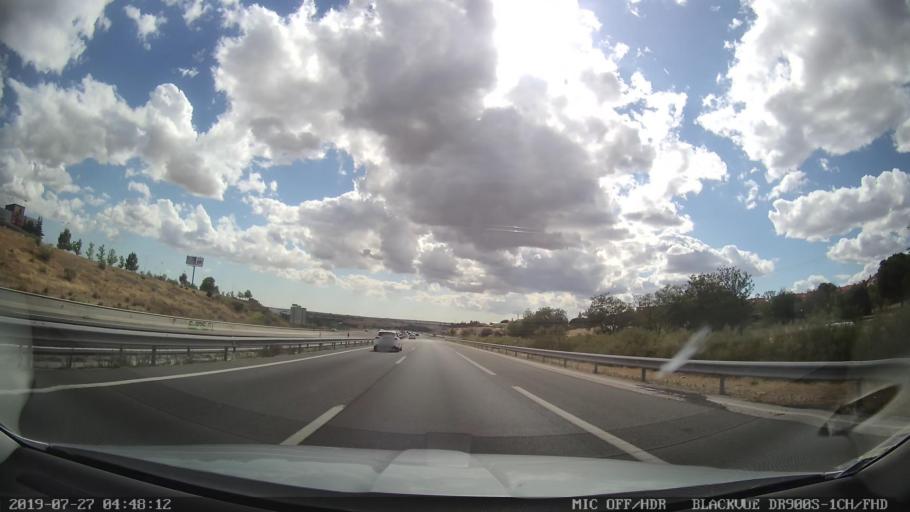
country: ES
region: Madrid
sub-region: Provincia de Madrid
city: Arroyomolinos
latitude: 40.3011
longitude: -3.9283
